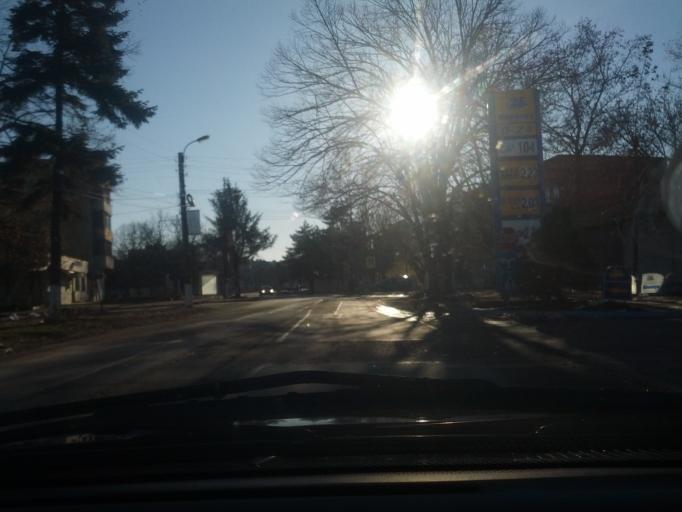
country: BG
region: Vratsa
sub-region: Obshtina Miziya
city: Miziya
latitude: 43.6932
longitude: 23.8130
